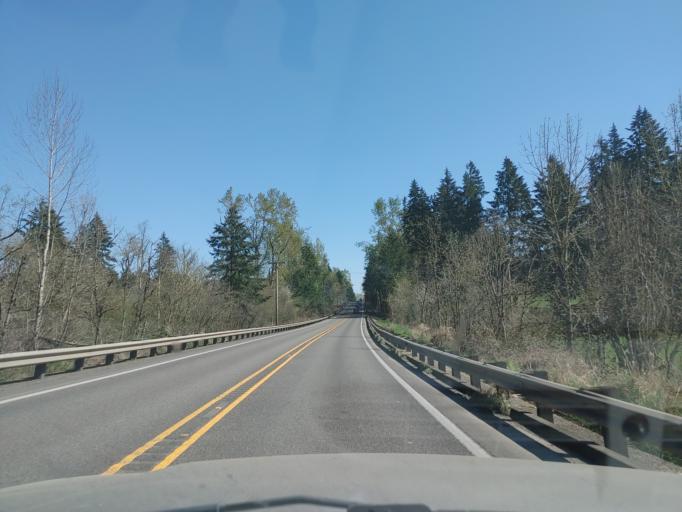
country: US
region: Oregon
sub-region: Marion County
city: Woodburn
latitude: 45.2335
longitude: -122.8932
